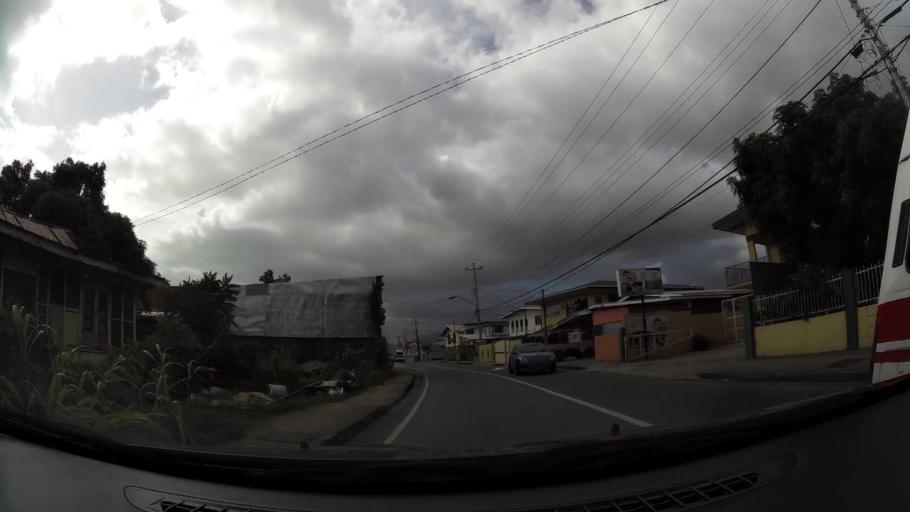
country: TT
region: Tunapuna/Piarco
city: Paradise
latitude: 10.6401
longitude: -61.3507
